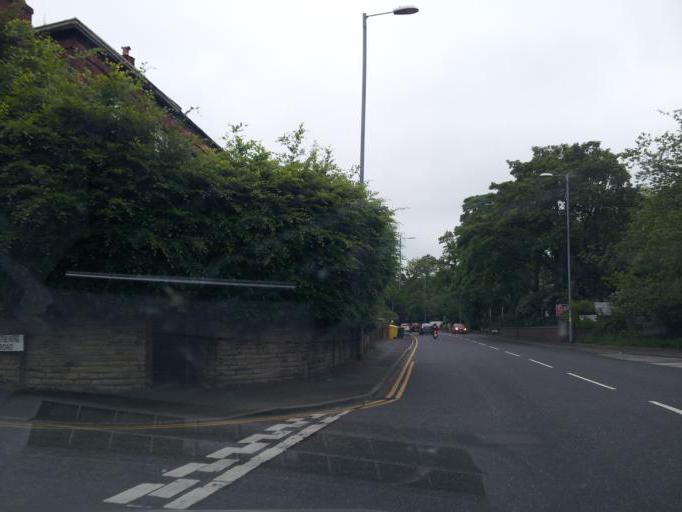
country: GB
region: England
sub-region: Manchester
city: Crumpsall
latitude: 53.5167
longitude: -2.2490
